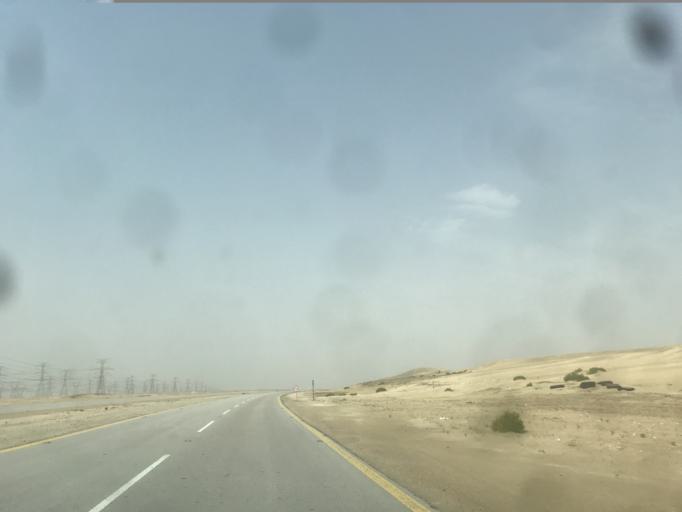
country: SA
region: Eastern Province
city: Abqaiq
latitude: 25.9075
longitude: 49.8921
